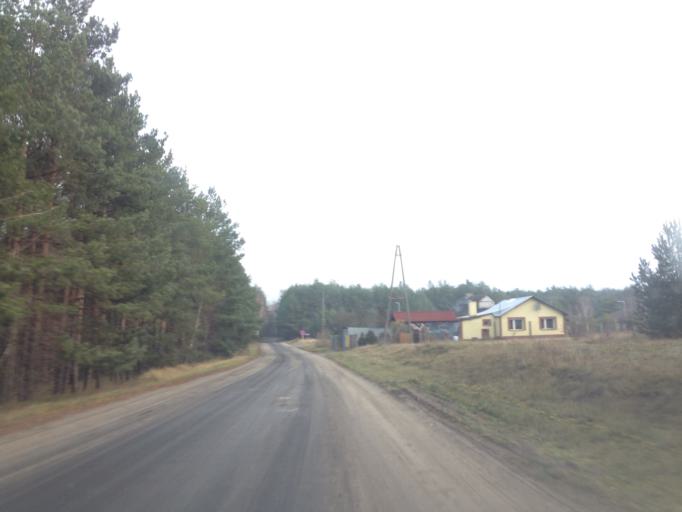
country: PL
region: Kujawsko-Pomorskie
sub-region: Powiat torunski
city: Wielka Nieszawka
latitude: 52.9946
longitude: 18.4485
